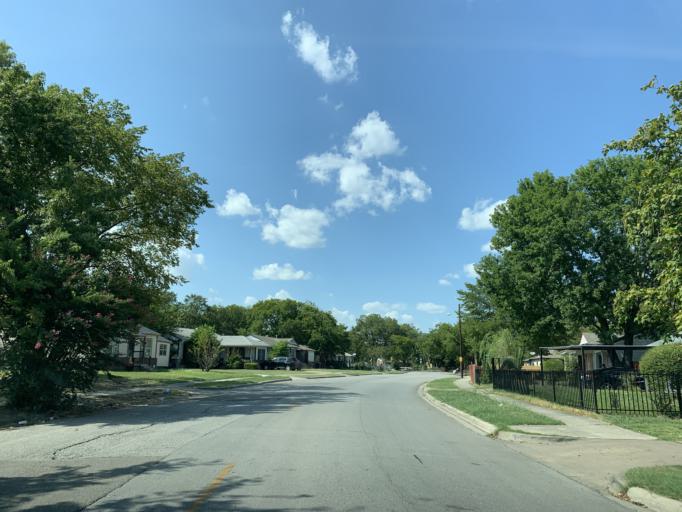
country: US
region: Texas
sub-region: Dallas County
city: Hutchins
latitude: 32.7025
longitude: -96.7717
